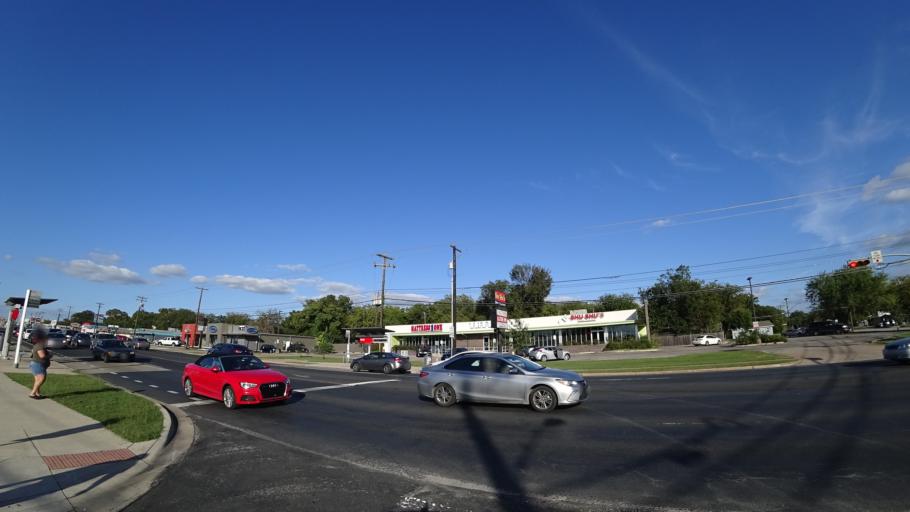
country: US
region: Texas
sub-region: Williamson County
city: Jollyville
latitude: 30.3633
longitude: -97.7291
